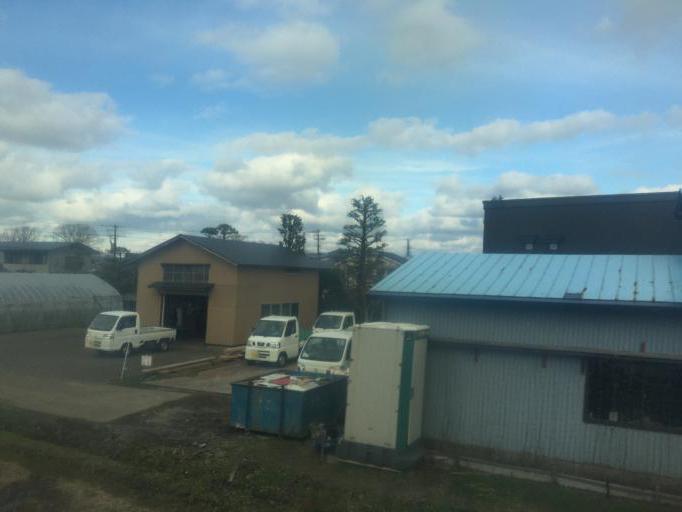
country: JP
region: Akita
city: Noshiromachi
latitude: 40.1952
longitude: 140.0888
